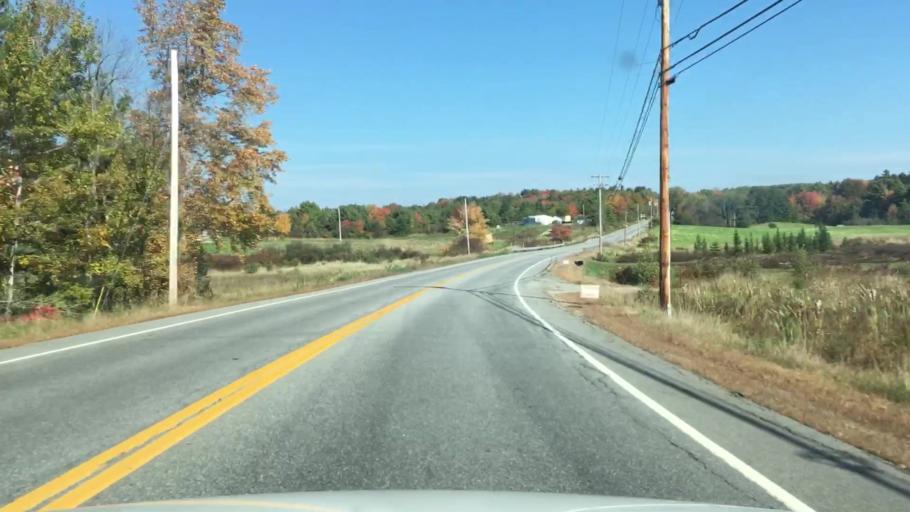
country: US
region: Maine
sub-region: Sagadahoc County
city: Topsham
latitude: 43.9808
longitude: -69.9607
